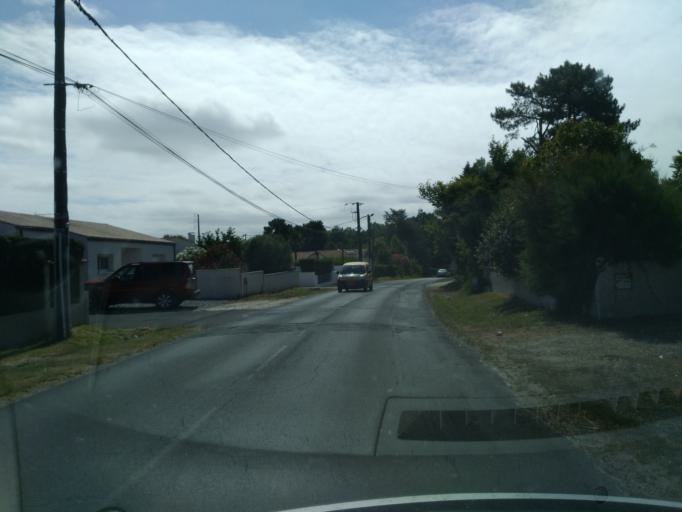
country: FR
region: Poitou-Charentes
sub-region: Departement de la Charente-Maritime
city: Saint-Palais-sur-Mer
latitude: 45.6675
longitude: -1.0807
